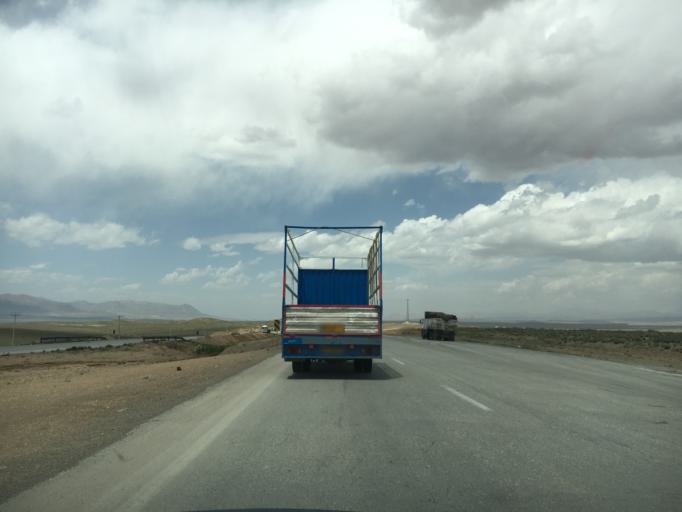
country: IR
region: Markazi
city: Delijan
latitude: 33.6663
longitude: 50.9593
